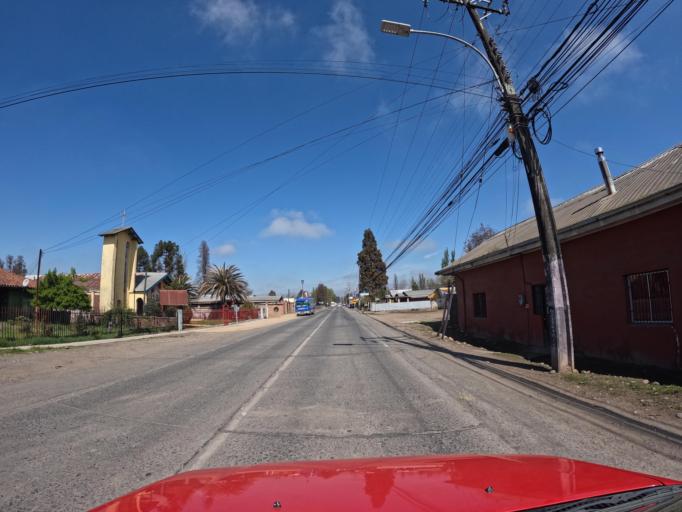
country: CL
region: Maule
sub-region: Provincia de Curico
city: Molina
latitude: -35.0792
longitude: -71.2612
